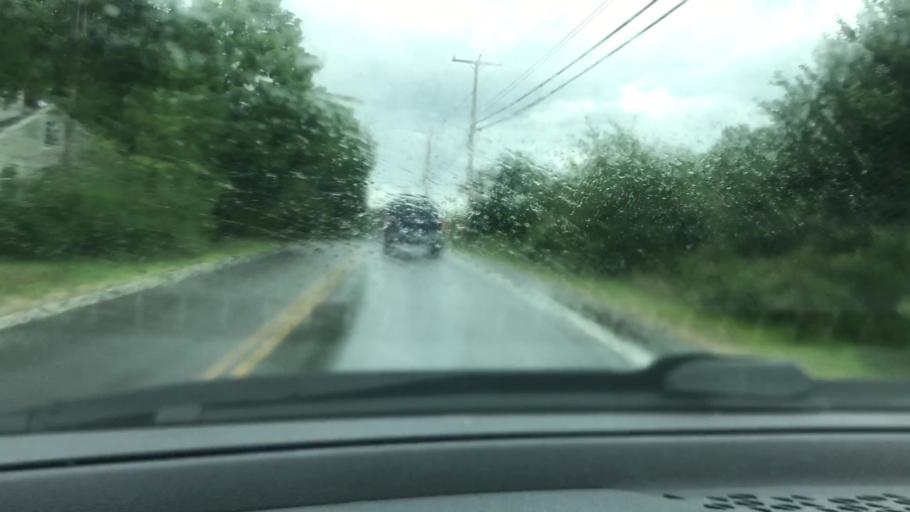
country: US
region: New Hampshire
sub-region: Merrimack County
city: Epsom
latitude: 43.1717
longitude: -71.2578
